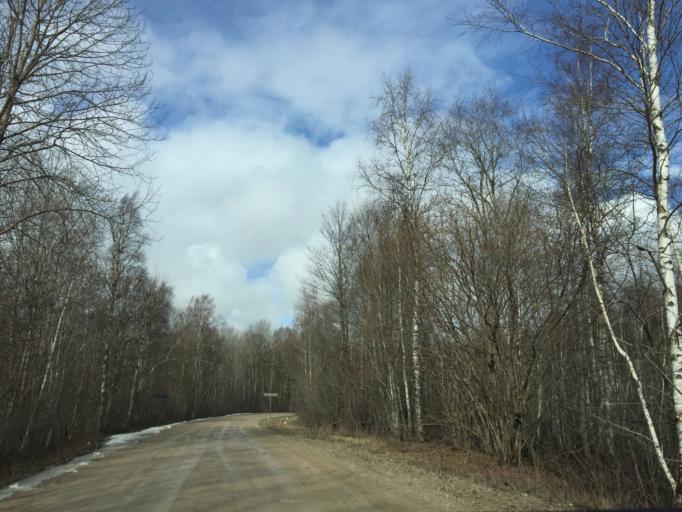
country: EE
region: Laeaene
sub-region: Lihula vald
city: Lihula
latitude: 58.7262
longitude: 23.8299
